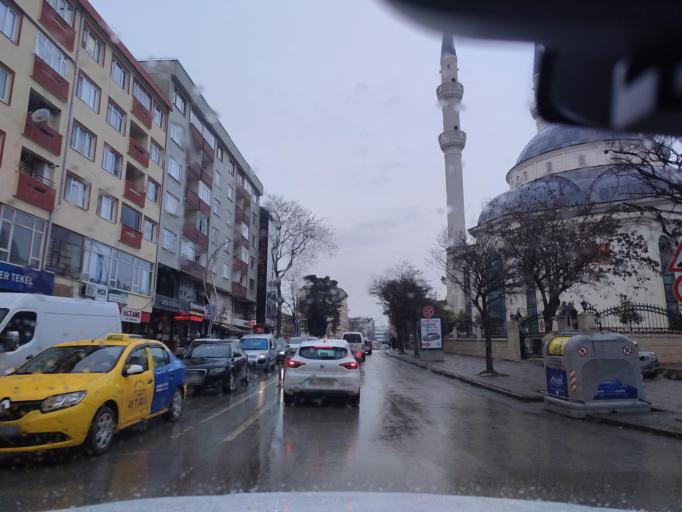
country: TR
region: Kocaeli
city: Gebze
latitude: 40.7991
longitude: 29.4402
